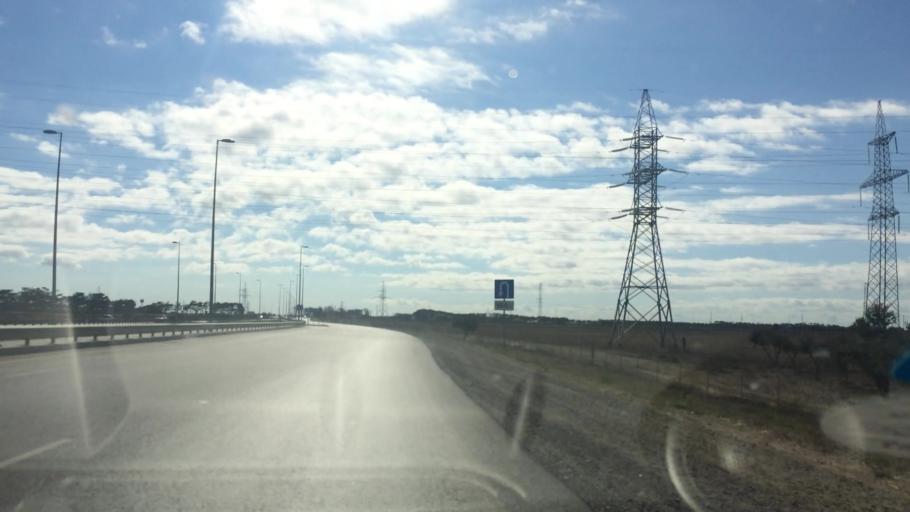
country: AZ
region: Baki
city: Qala
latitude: 40.4374
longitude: 50.1839
